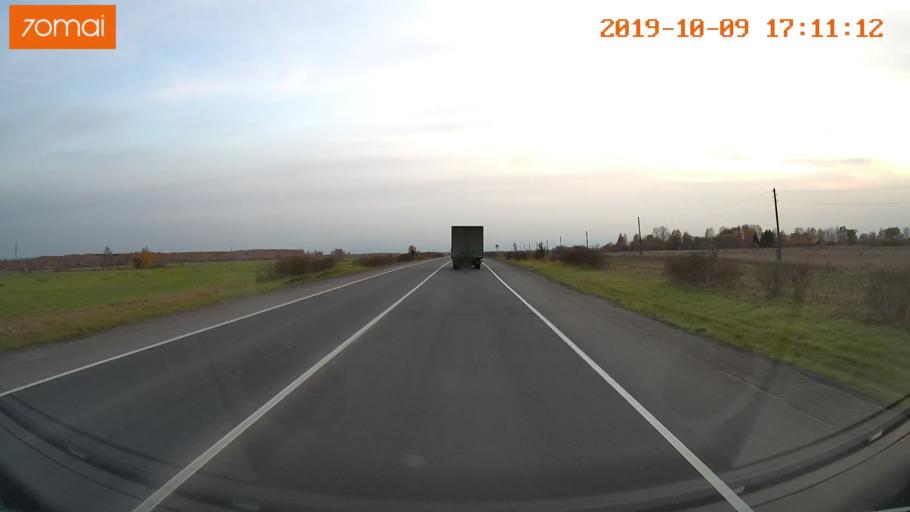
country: RU
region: Ivanovo
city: Privolzhsk
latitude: 57.3461
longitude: 41.2517
